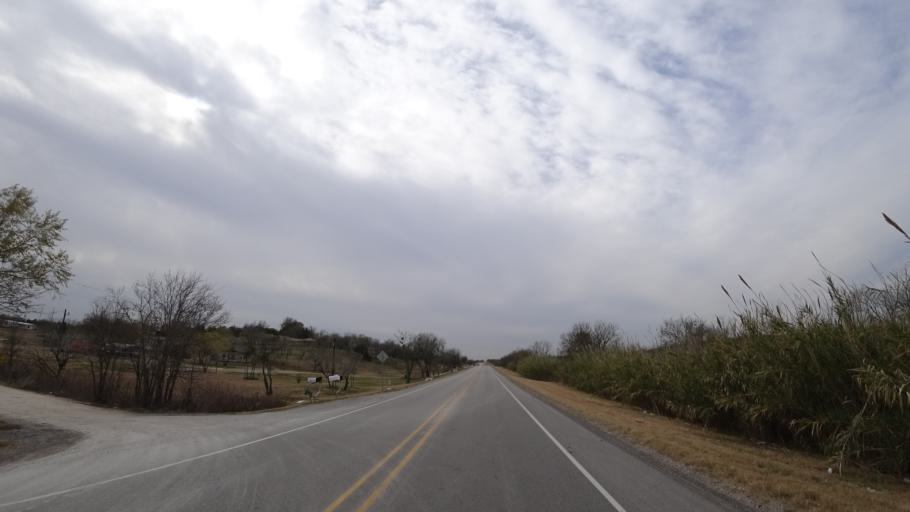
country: US
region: Texas
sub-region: Travis County
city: Onion Creek
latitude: 30.1333
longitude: -97.6818
